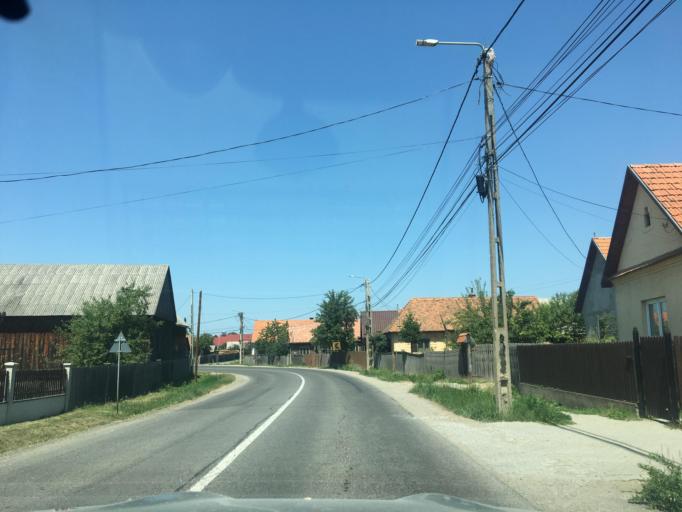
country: RO
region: Harghita
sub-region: Comuna Joseni
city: Joseni
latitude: 46.7029
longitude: 25.4949
